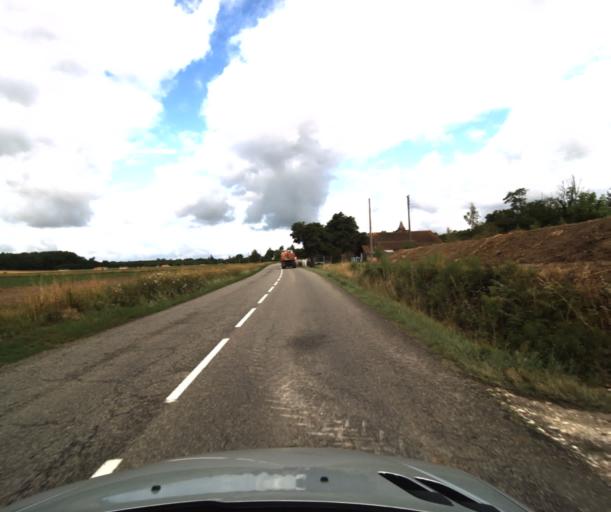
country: FR
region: Midi-Pyrenees
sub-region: Departement du Tarn-et-Garonne
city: Castelsarrasin
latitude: 44.0256
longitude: 1.0602
